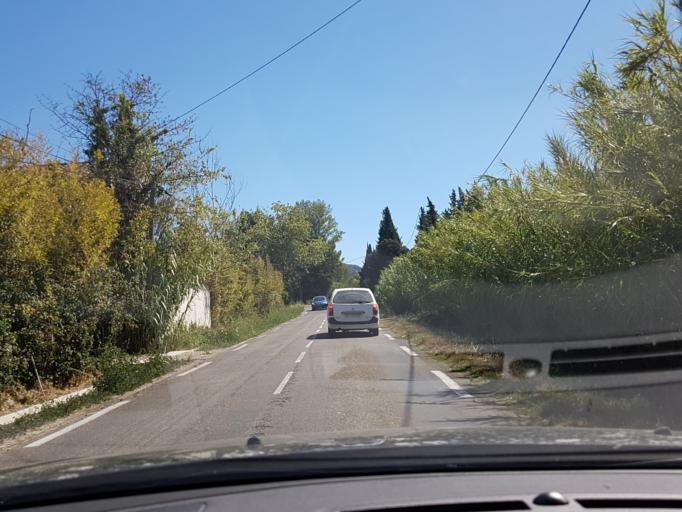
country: FR
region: Provence-Alpes-Cote d'Azur
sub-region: Departement des Bouches-du-Rhone
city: Eygalieres
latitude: 43.7742
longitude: 4.9306
